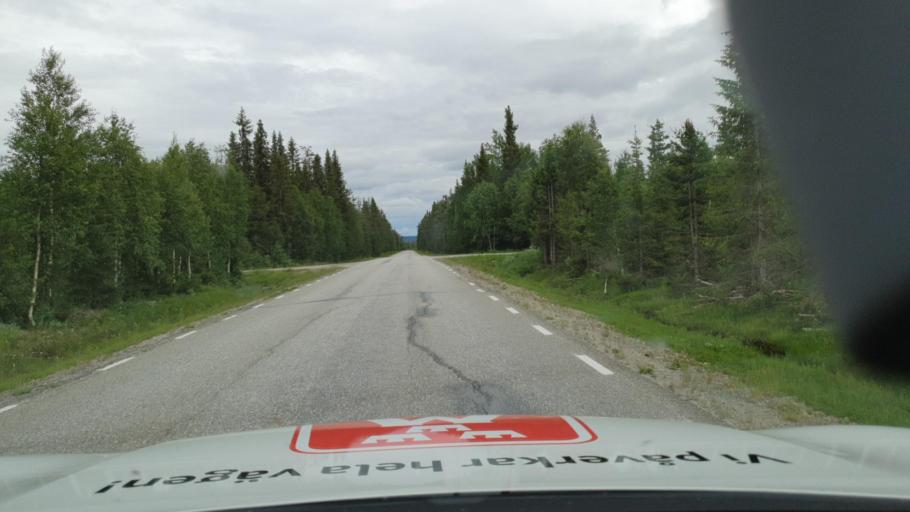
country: SE
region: Vaesterbotten
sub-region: Lycksele Kommun
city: Soderfors
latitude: 64.3129
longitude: 18.1617
